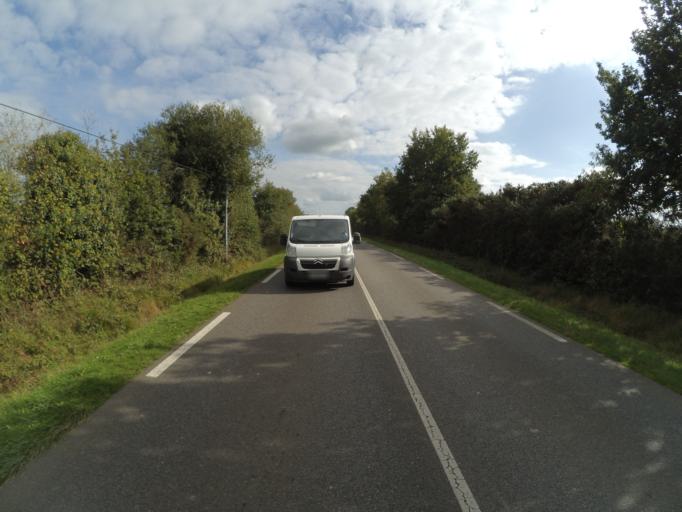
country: FR
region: Pays de la Loire
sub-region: Departement de la Loire-Atlantique
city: Guenrouet
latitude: 47.5484
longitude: -1.9466
